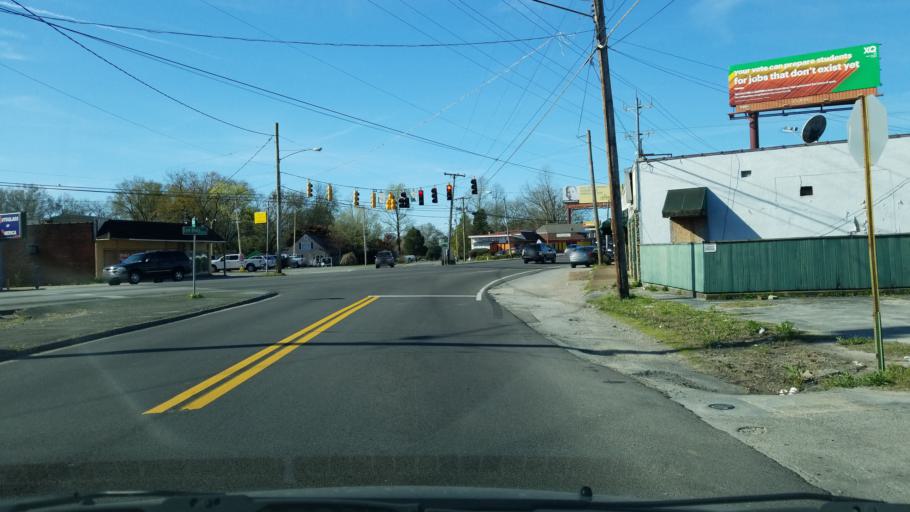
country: US
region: Tennessee
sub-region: Hamilton County
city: East Ridge
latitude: 35.0227
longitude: -85.1984
